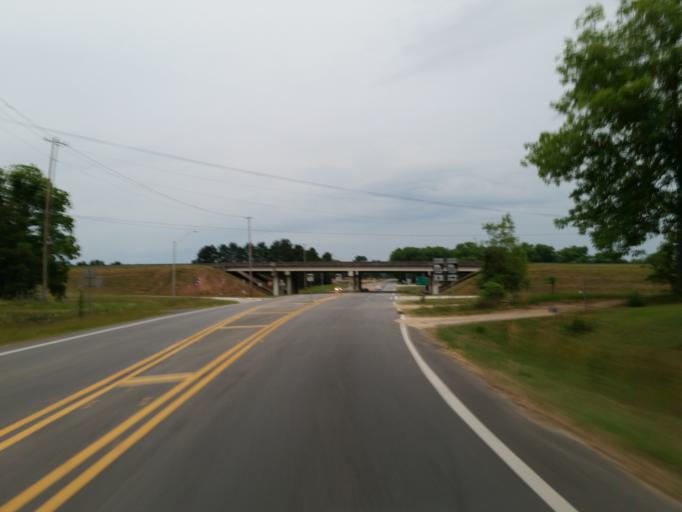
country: US
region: Georgia
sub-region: Crisp County
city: Cordele
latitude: 31.9248
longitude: -83.7726
